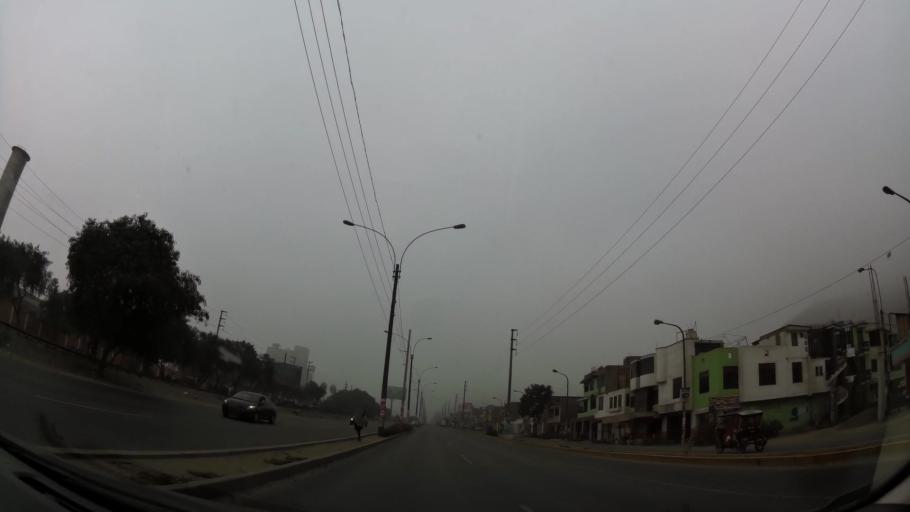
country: PE
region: Lima
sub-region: Lima
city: Chaclacayo
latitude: -11.9928
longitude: -76.8265
